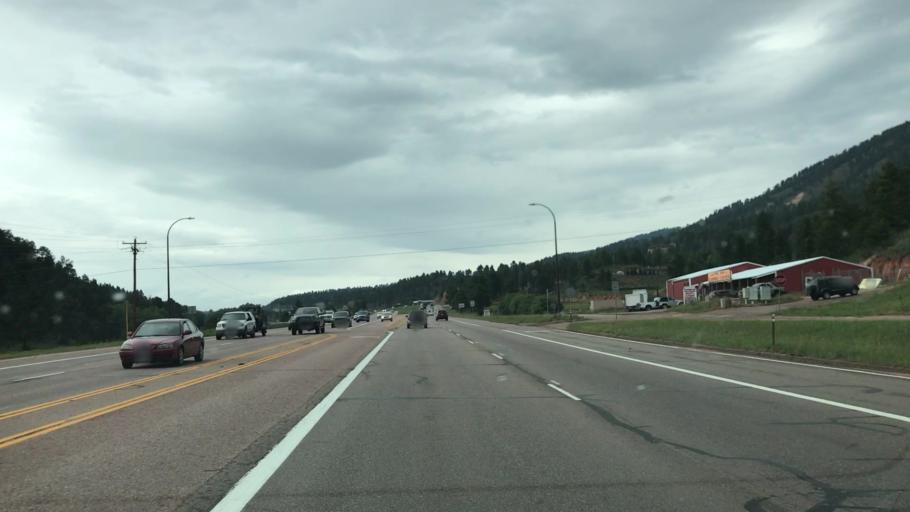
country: US
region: Colorado
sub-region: El Paso County
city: Cascade-Chipita Park
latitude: 38.9564
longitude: -105.0276
